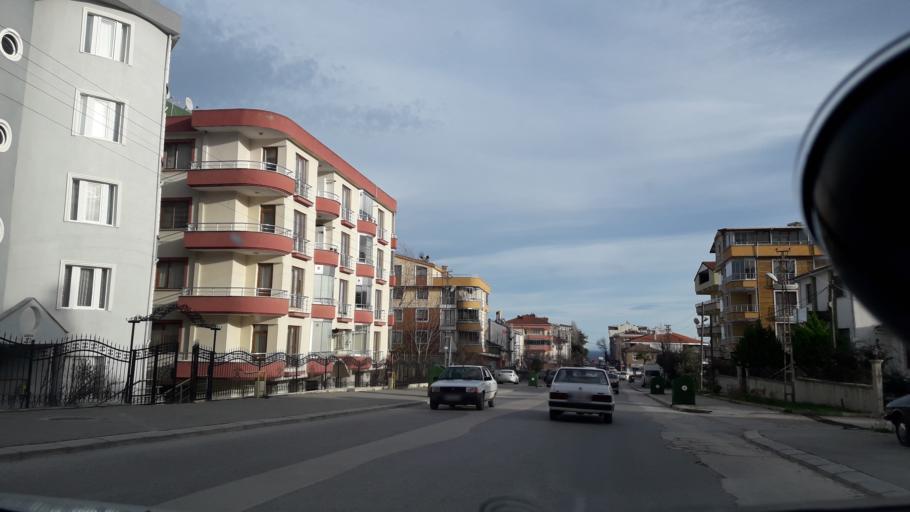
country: TR
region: Sinop
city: Gerze
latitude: 41.8068
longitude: 35.1883
